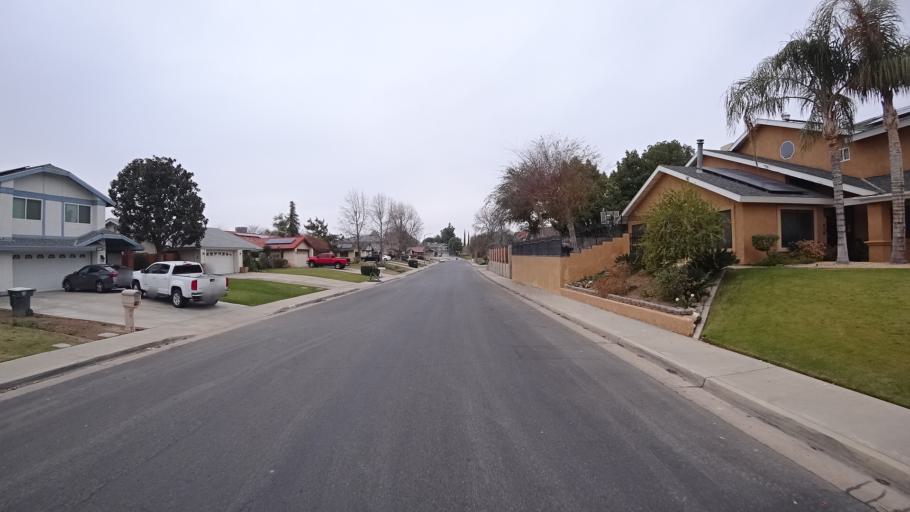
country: US
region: California
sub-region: Kern County
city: Bakersfield
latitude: 35.3801
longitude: -118.9345
